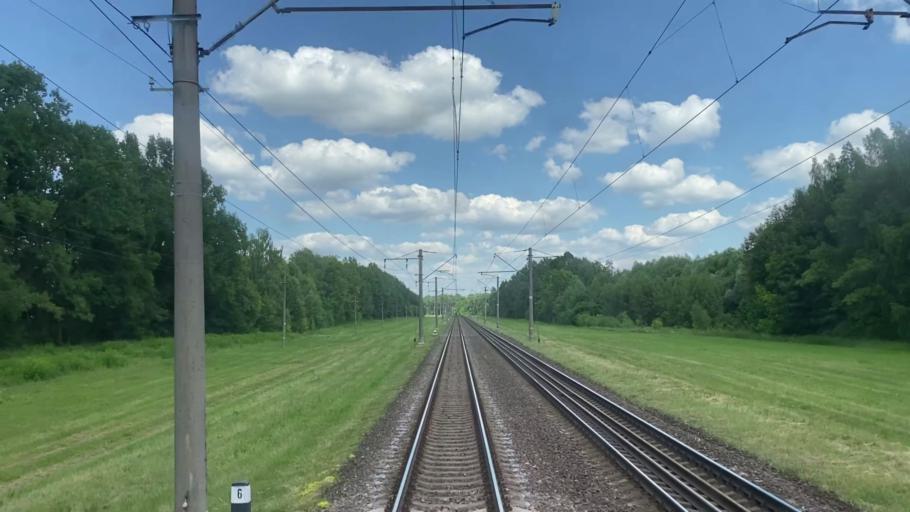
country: BY
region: Brest
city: Zhabinka
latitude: 52.2685
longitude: 24.1504
